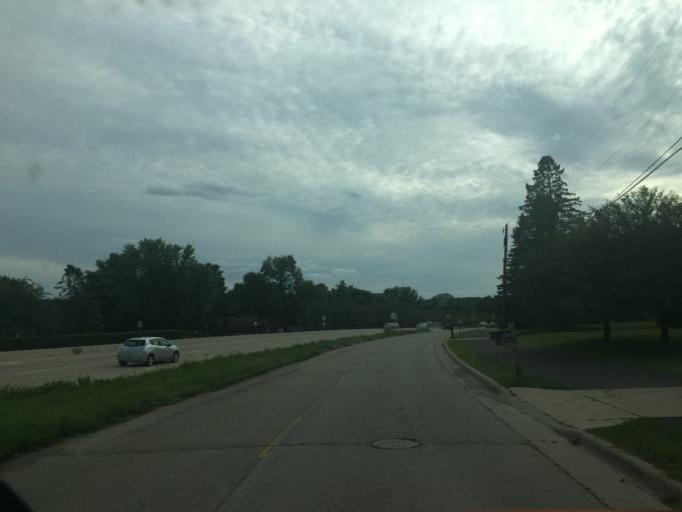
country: US
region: Minnesota
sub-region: Olmsted County
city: Rochester
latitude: 44.0003
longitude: -92.4922
